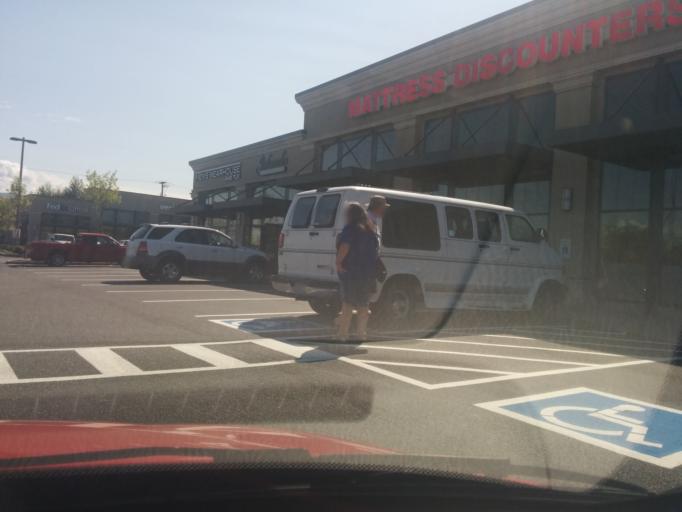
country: US
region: Washington
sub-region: Skagit County
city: Burlington
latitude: 48.4514
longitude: -122.3368
